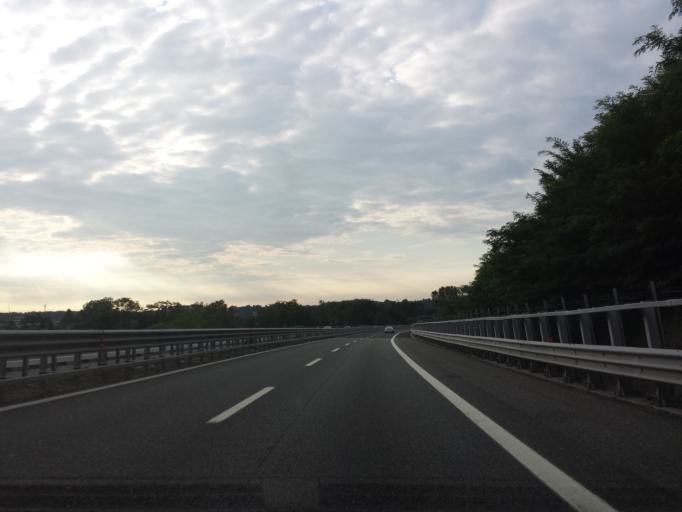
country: IT
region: Lombardy
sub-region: Provincia di Varese
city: Cavaria Con Premezzo
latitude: 45.6846
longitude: 8.7890
